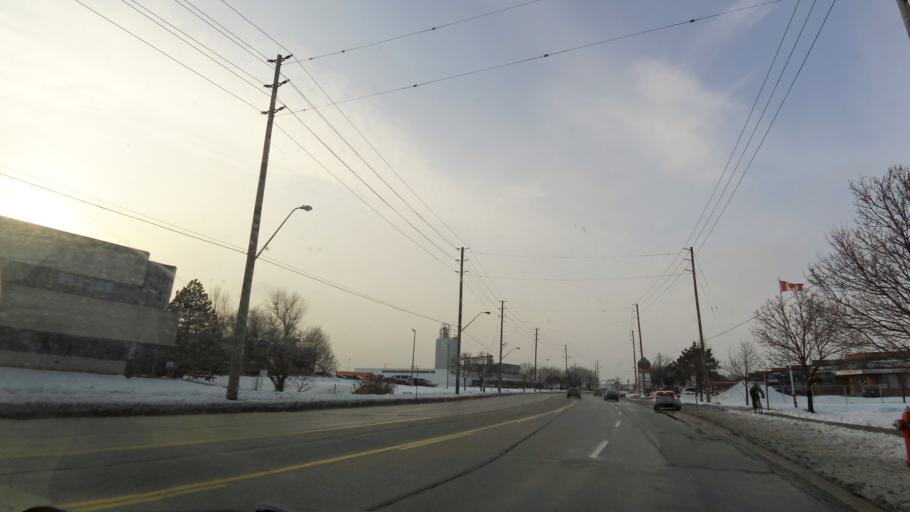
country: CA
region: Ontario
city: Brampton
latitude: 43.7035
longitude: -79.7246
